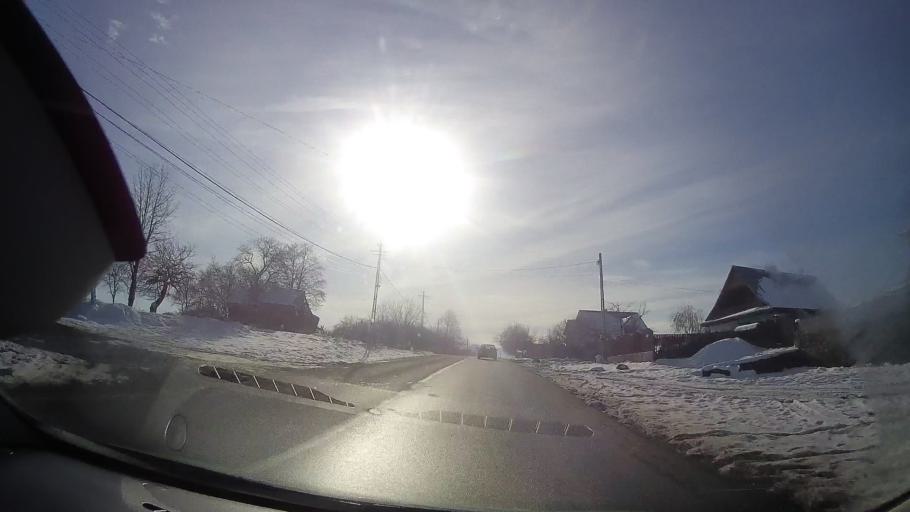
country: RO
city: Vanatori-Neamt
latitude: 47.1807
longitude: 26.3304
